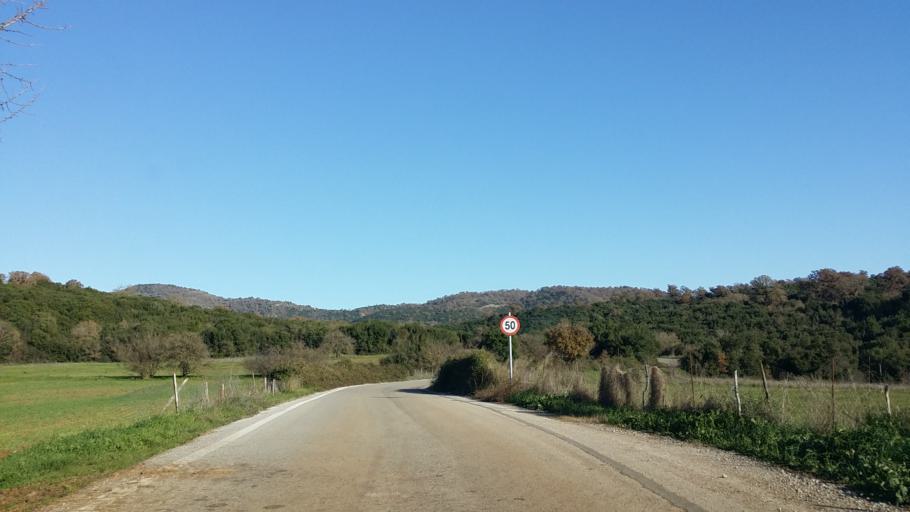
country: GR
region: West Greece
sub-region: Nomos Aitolias kai Akarnanias
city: Fitiai
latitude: 38.6342
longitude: 21.1623
